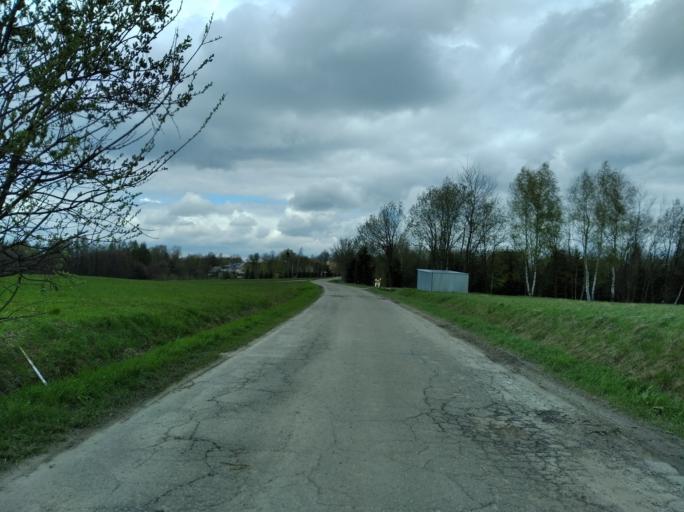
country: PL
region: Subcarpathian Voivodeship
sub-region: Powiat rzeszowski
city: Lubenia
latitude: 49.8898
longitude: 21.9322
